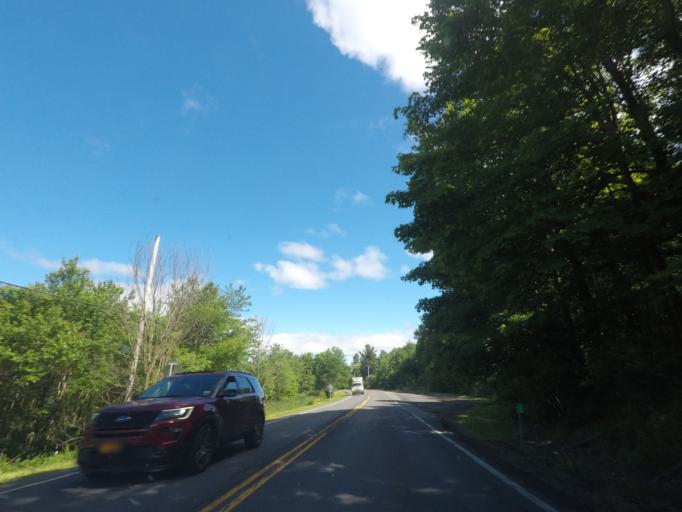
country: US
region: New York
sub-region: Columbia County
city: Philmont
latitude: 42.1897
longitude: -73.6198
